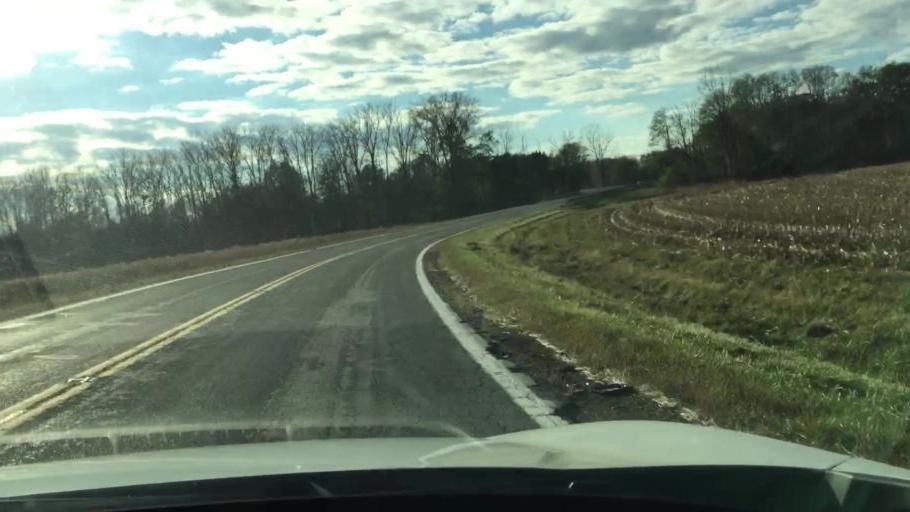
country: US
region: Ohio
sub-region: Champaign County
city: North Lewisburg
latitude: 40.2280
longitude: -83.5188
